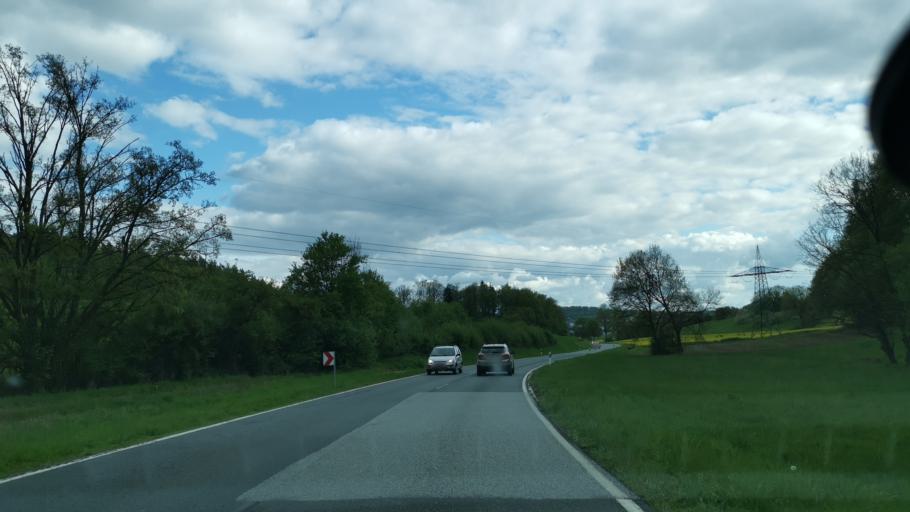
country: DE
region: Baden-Wuerttemberg
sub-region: Karlsruhe Region
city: Osterburken
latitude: 49.4485
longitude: 9.4267
